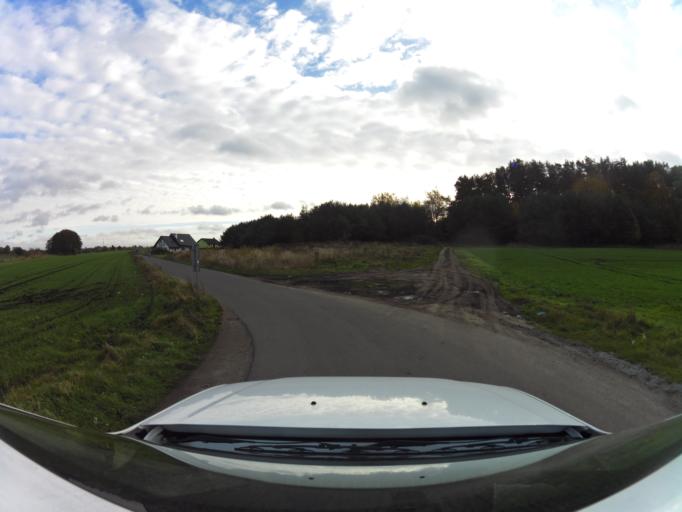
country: PL
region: West Pomeranian Voivodeship
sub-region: Powiat gryficki
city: Gryfice
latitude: 53.9110
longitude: 15.1740
